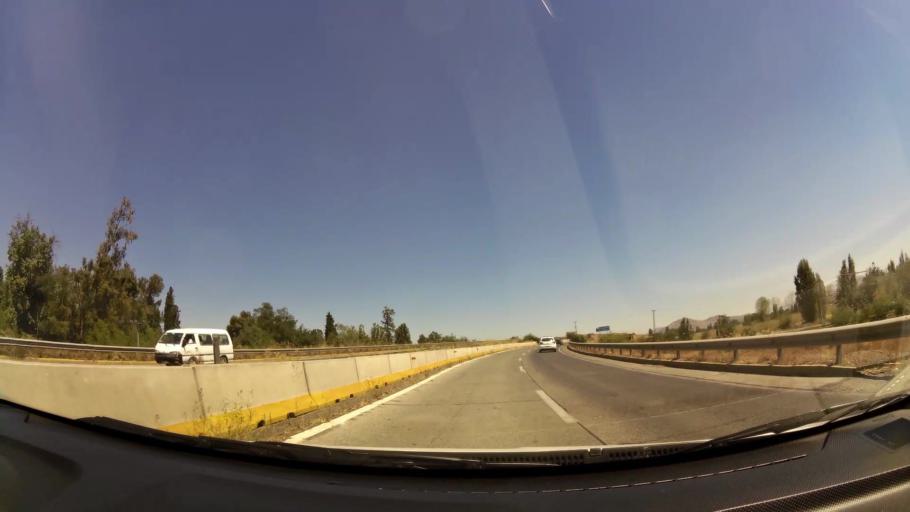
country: CL
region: O'Higgins
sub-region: Provincia de Cachapoal
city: Rancagua
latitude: -34.2305
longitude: -70.7855
